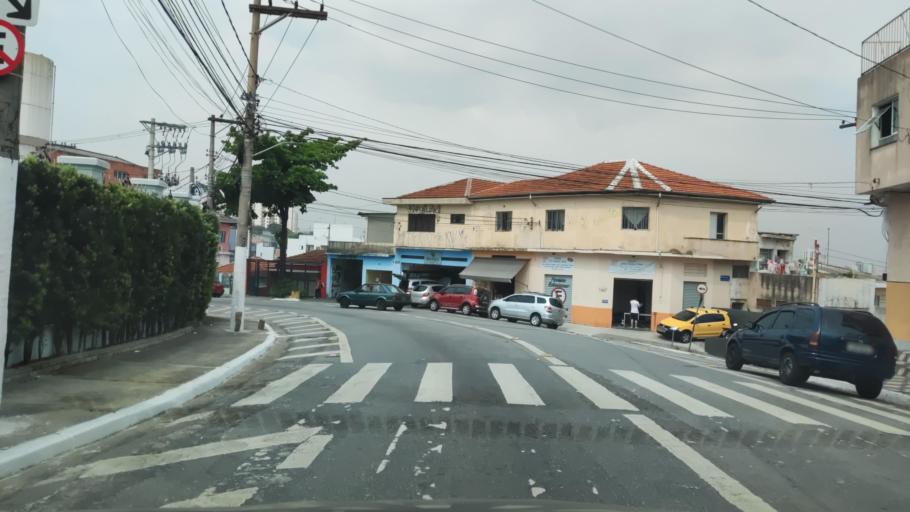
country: BR
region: Sao Paulo
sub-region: Sao Paulo
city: Sao Paulo
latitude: -23.4932
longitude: -46.6787
